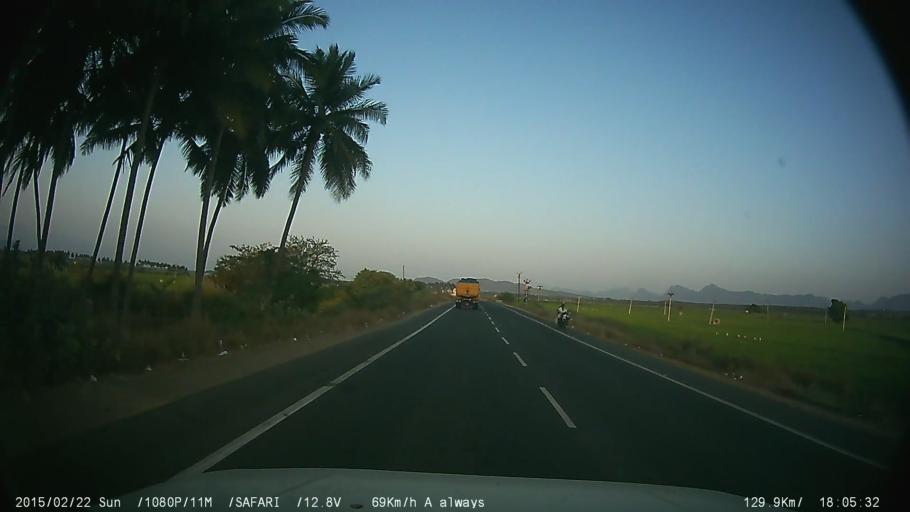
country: IN
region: Tamil Nadu
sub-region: Theni
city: Chinnamanur
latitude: 9.8240
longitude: 77.3572
